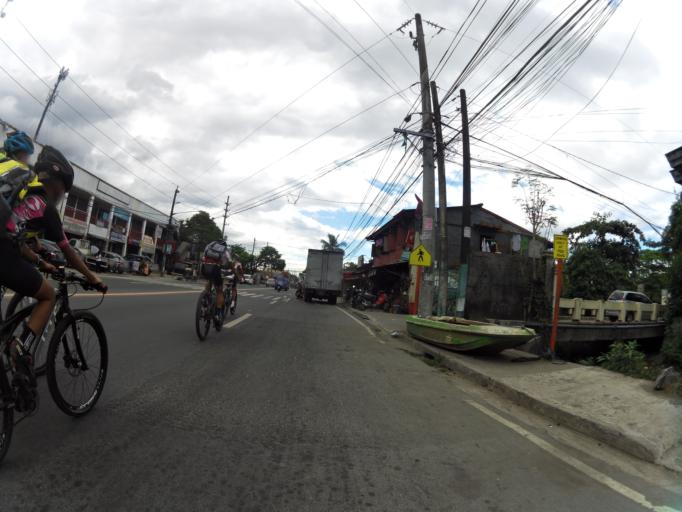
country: PH
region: Calabarzon
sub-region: Province of Rizal
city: Antipolo
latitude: 14.6324
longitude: 121.1146
